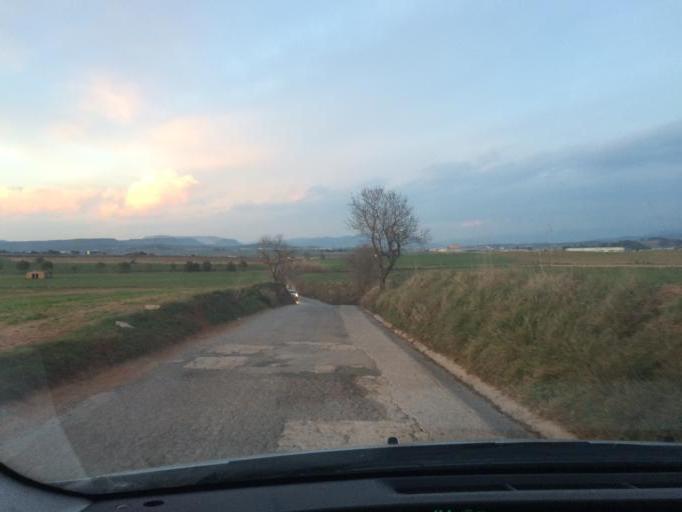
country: ES
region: Catalonia
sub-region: Provincia de Barcelona
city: Sant Fruitos de Bages
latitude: 41.7500
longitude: 1.8489
